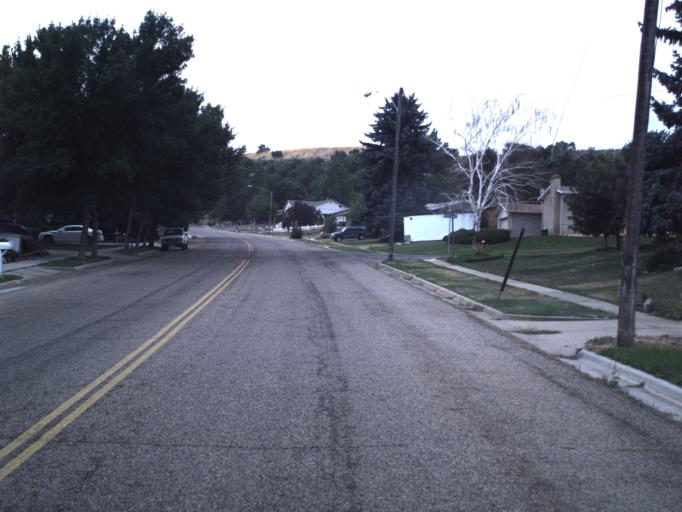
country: US
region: Utah
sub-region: Weber County
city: Riverdale
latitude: 41.1635
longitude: -112.0081
